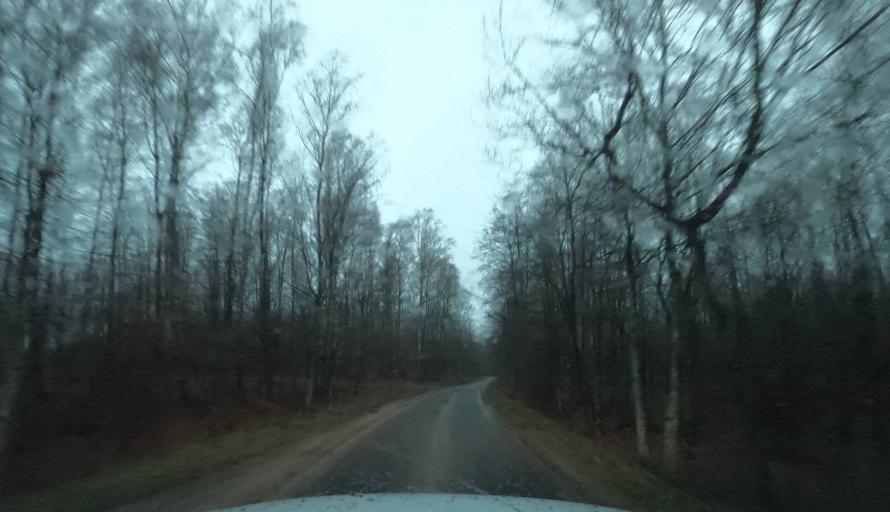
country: PL
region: West Pomeranian Voivodeship
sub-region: Powiat szczecinecki
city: Borne Sulinowo
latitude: 53.6921
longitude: 16.4848
